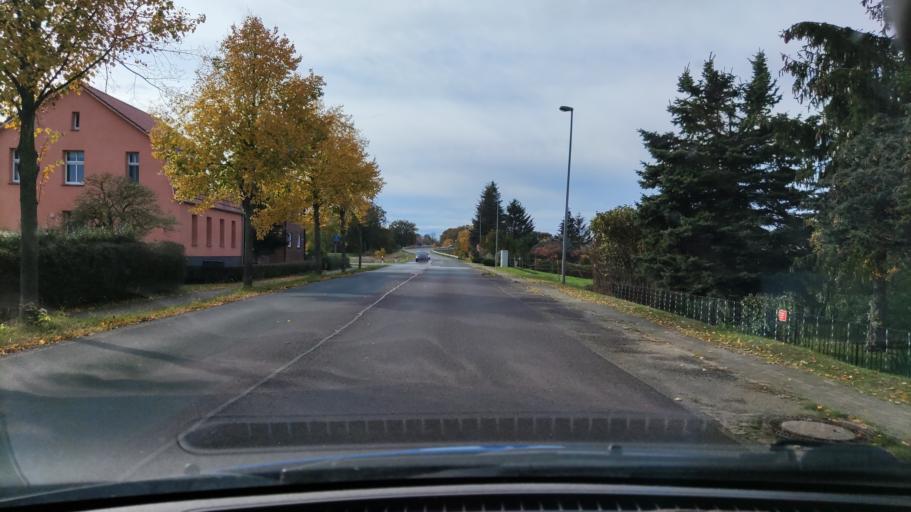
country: DE
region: Brandenburg
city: Weisen
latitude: 53.0215
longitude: 11.7753
